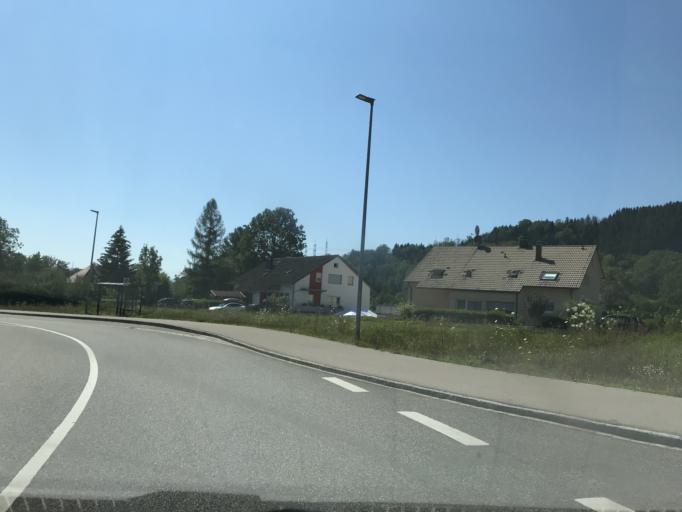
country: DE
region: Baden-Wuerttemberg
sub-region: Freiburg Region
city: Wehr
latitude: 47.6160
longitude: 7.9076
